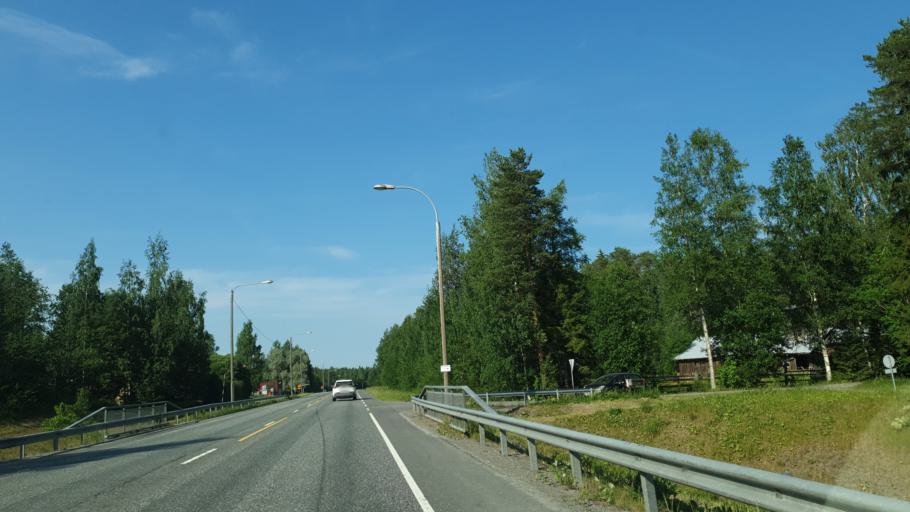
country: FI
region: Northern Savo
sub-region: Kuopio
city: Siilinjaervi
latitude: 63.1259
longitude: 27.7716
